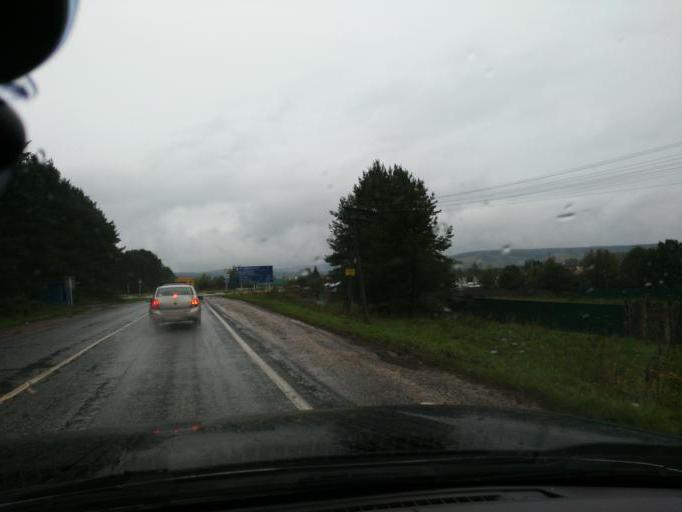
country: RU
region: Perm
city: Yugo-Kamskiy
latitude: 57.6863
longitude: 55.5680
